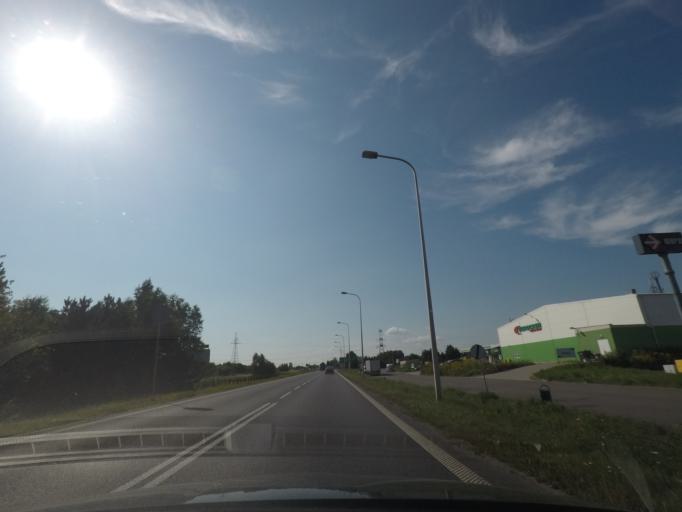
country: PL
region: Silesian Voivodeship
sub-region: Zory
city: Zory
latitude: 50.0603
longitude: 18.6687
